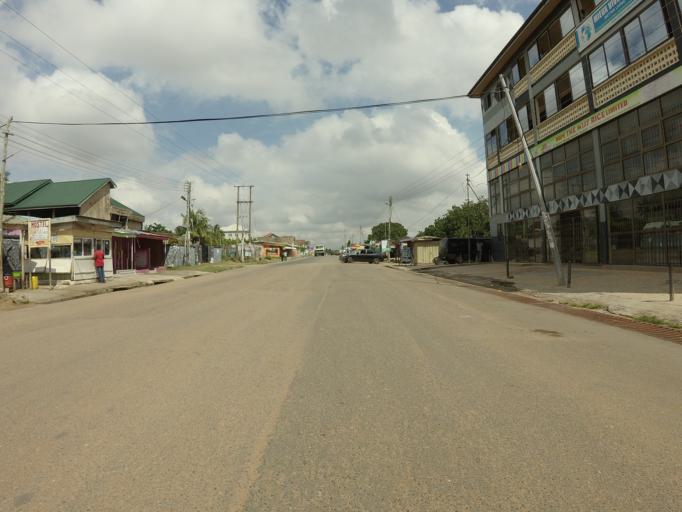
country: GH
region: Greater Accra
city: Nungua
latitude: 5.6123
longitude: -0.0821
